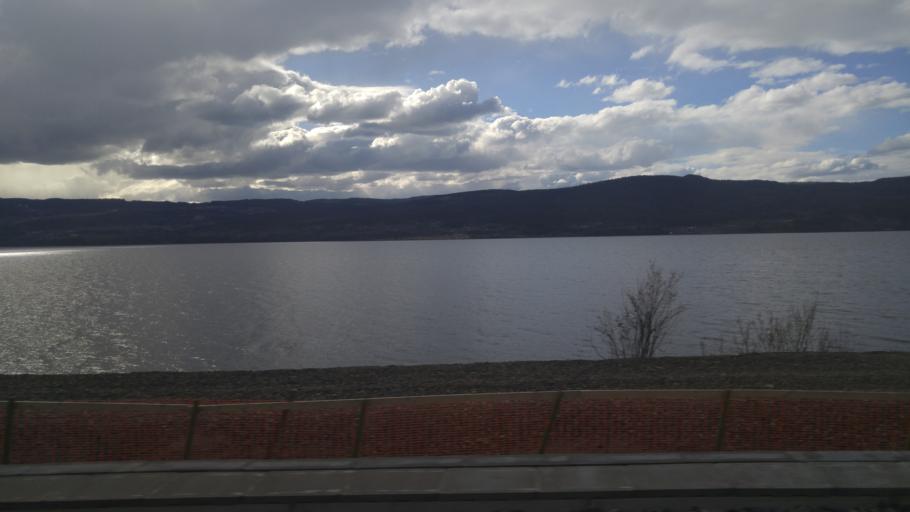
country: NO
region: Akershus
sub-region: Eidsvoll
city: Eidsvoll
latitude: 60.5111
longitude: 11.2423
